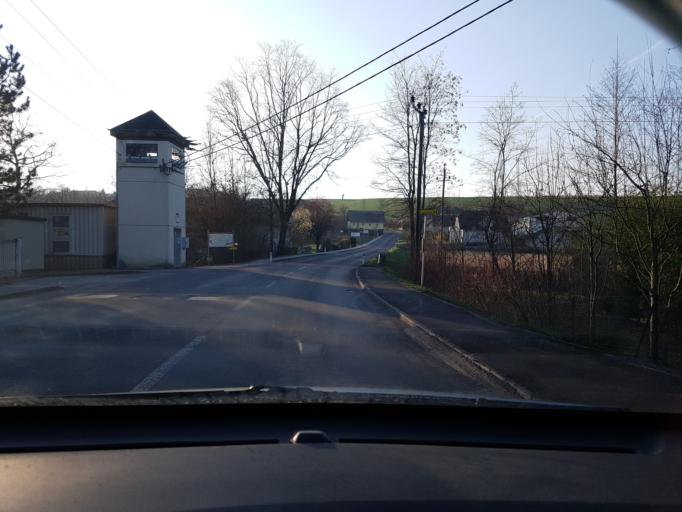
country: AT
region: Upper Austria
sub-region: Politischer Bezirk Linz-Land
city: Sankt Florian
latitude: 48.1638
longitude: 14.3380
